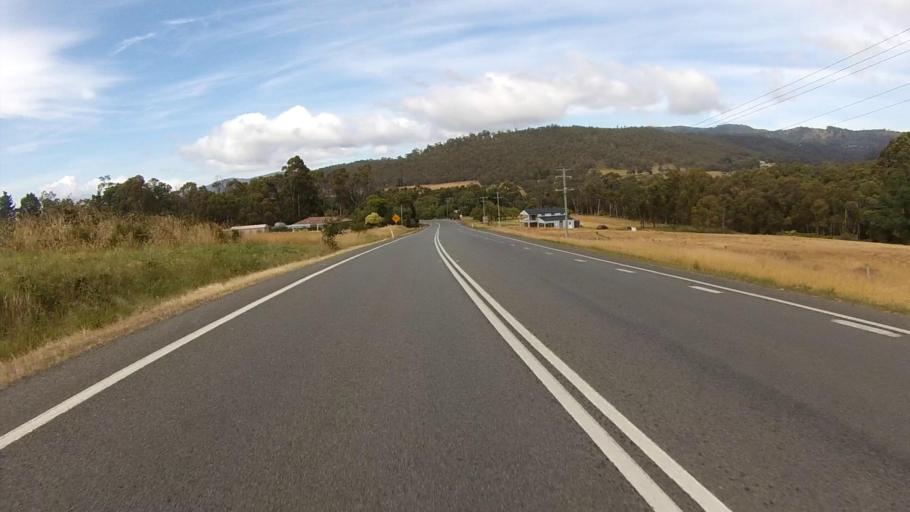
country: AU
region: Tasmania
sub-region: Kingborough
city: Kettering
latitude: -43.1163
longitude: 147.2448
